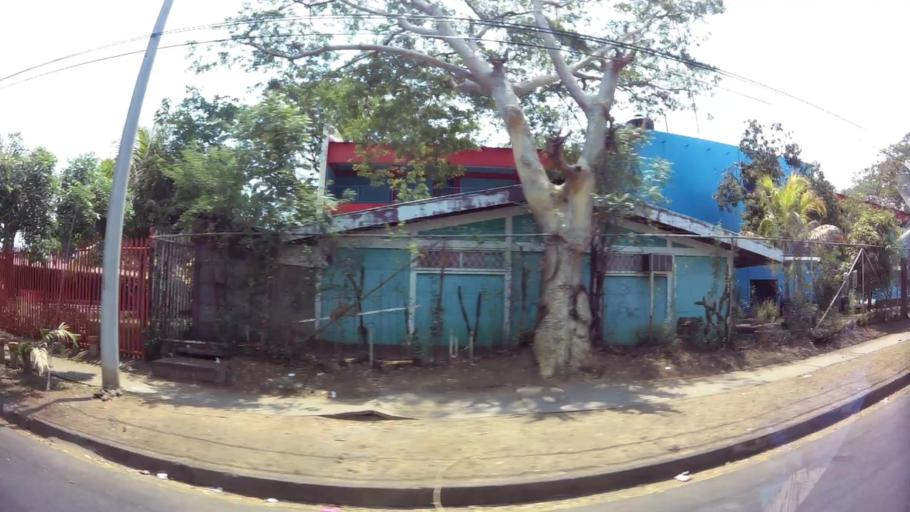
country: NI
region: Managua
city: Ciudad Sandino
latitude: 12.1540
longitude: -86.3103
